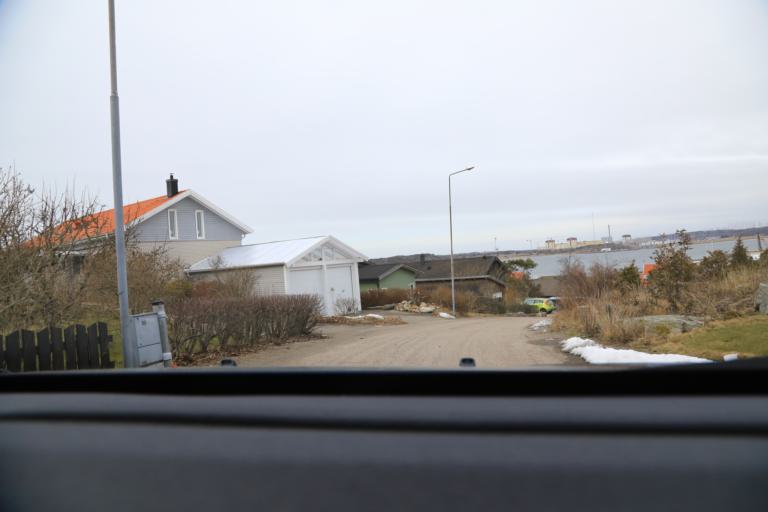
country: SE
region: Halland
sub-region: Kungsbacka Kommun
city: Frillesas
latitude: 57.2375
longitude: 12.1095
